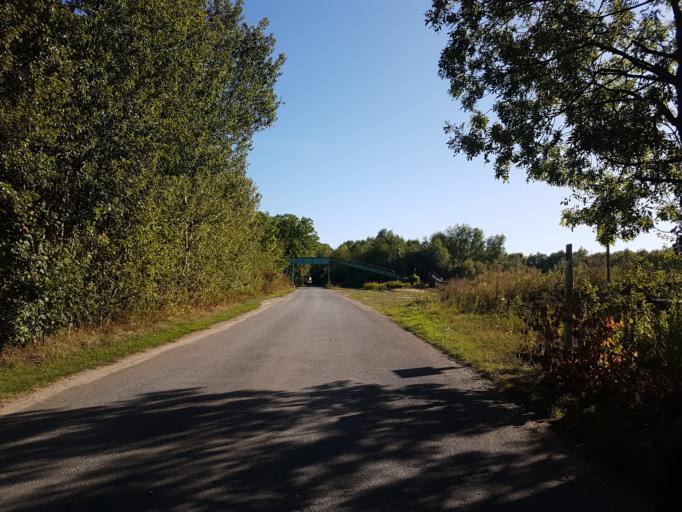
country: DE
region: North Rhine-Westphalia
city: Porta Westfalica
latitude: 52.2565
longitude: 8.9228
